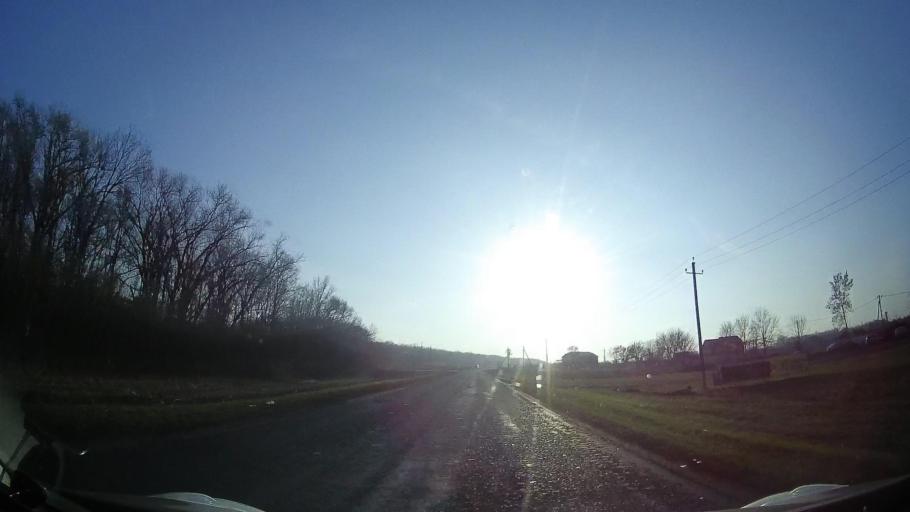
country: RU
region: Rostov
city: Ol'ginskaya
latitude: 47.1386
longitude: 39.8970
